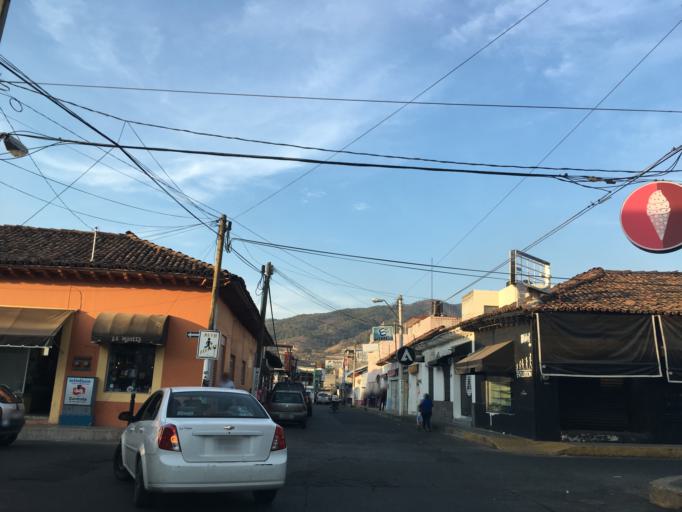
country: MX
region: Michoacan
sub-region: Los Reyes
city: La Higuerita (Colonia San Rafael)
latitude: 19.5893
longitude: -102.4729
